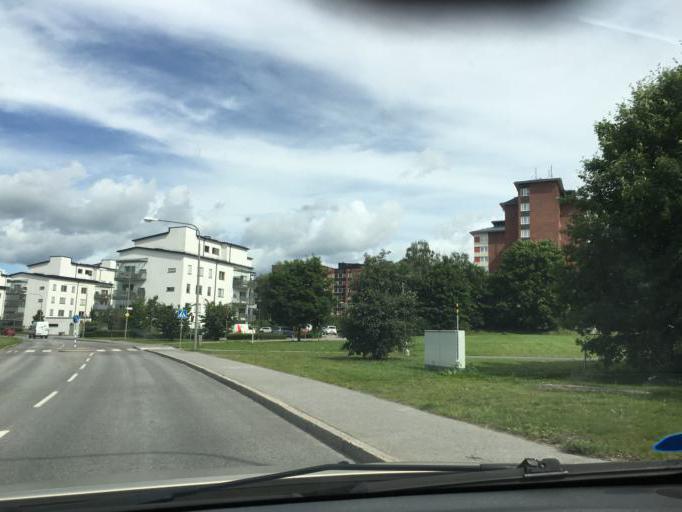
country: SE
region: Stockholm
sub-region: Stockholms Kommun
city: Bromma
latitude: 59.3614
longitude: 17.8937
